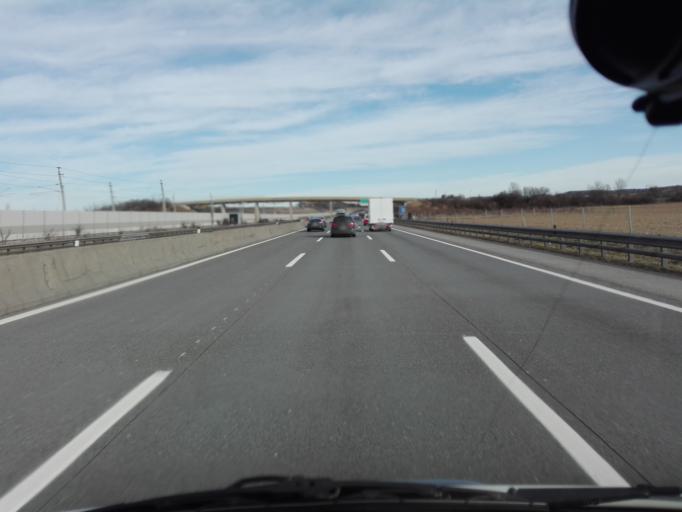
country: AT
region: Lower Austria
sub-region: Politischer Bezirk Sankt Polten
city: Gerersdorf
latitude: 48.1754
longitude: 15.5317
